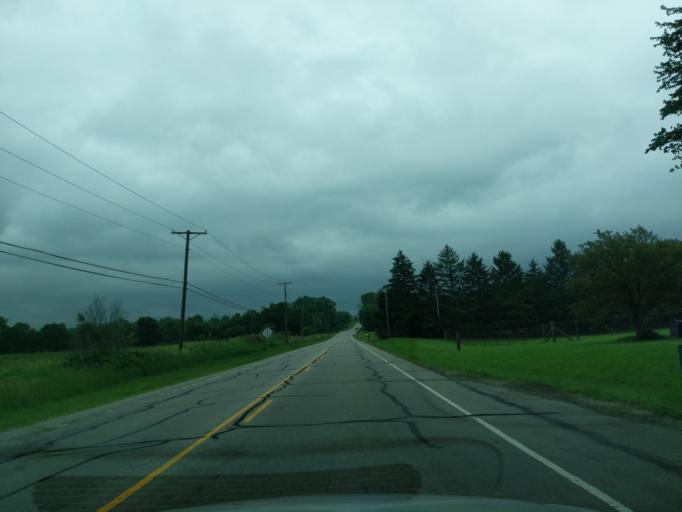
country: US
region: Indiana
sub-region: Madison County
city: Alexandria
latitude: 40.2778
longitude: -85.6473
